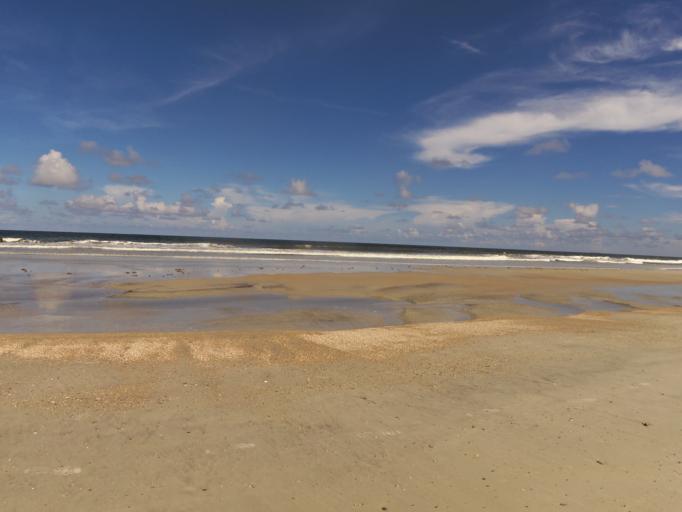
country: US
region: Florida
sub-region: Duval County
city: Atlantic Beach
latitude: 30.4686
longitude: -81.4120
